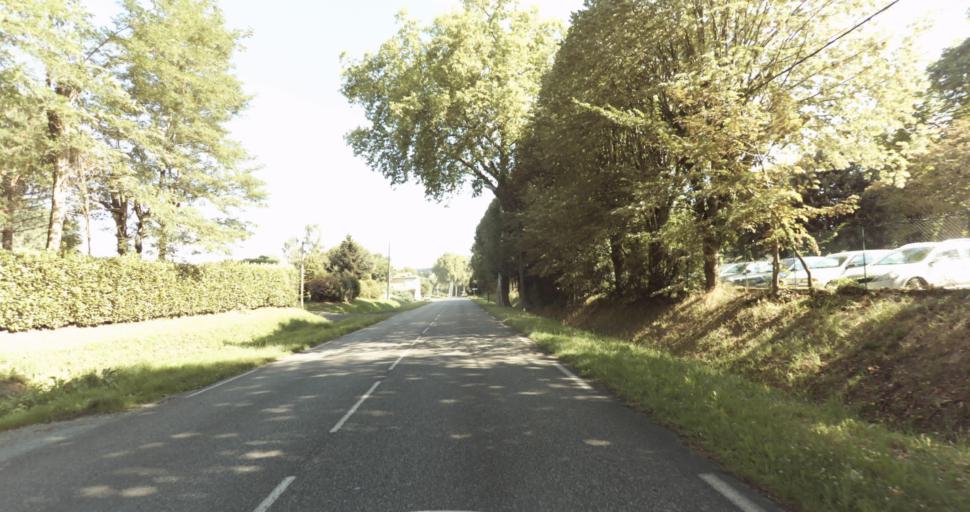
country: FR
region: Aquitaine
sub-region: Departement de la Gironde
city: Bazas
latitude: 44.4263
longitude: -0.2149
